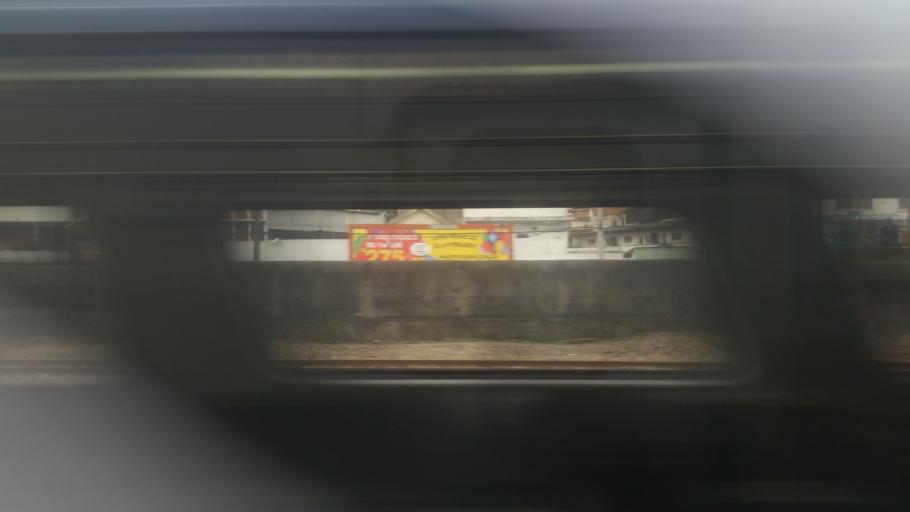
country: BR
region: Rio de Janeiro
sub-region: Sao Joao De Meriti
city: Sao Joao de Meriti
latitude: -22.8782
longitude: -43.3352
